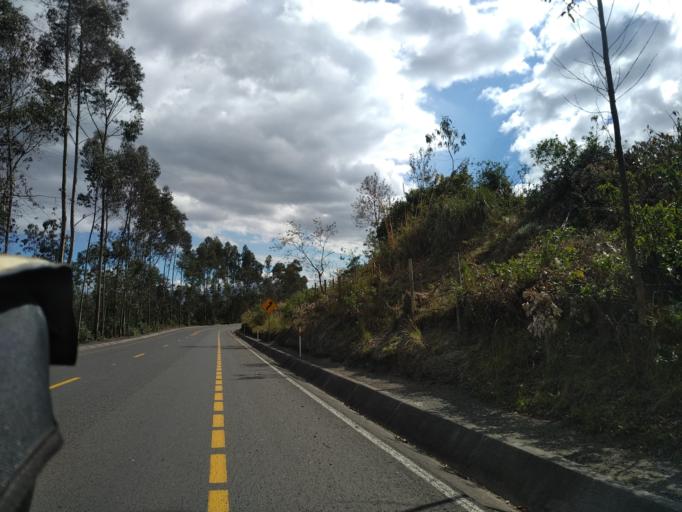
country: EC
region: Cotopaxi
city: Saquisili
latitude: -0.7002
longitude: -78.5773
